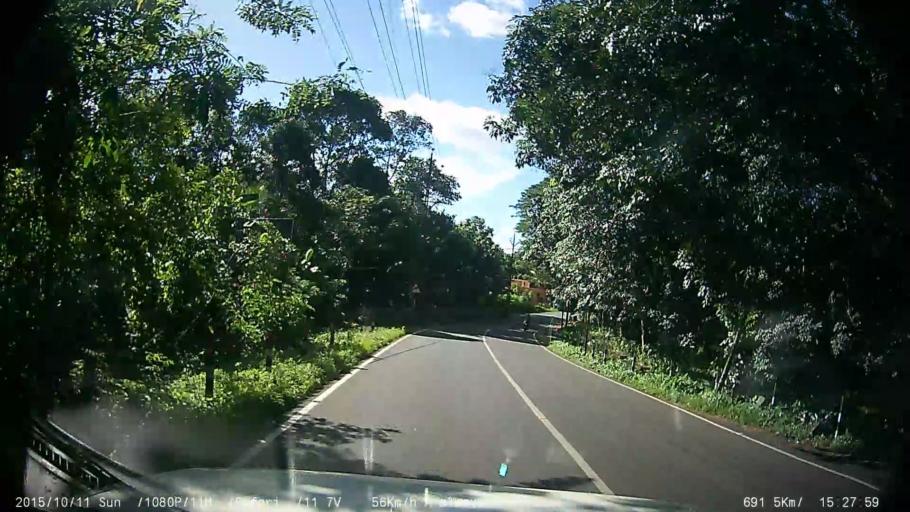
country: IN
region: Kerala
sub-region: Kottayam
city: Changanacheri
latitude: 9.4845
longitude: 76.5731
